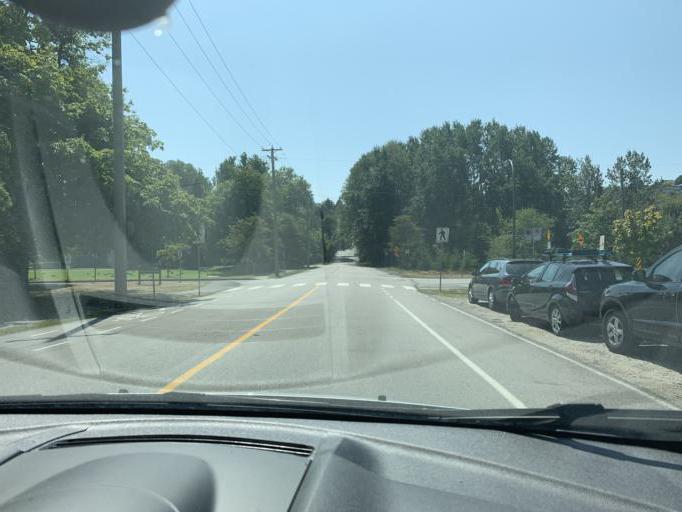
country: CA
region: British Columbia
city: West End
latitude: 49.2740
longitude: -123.2057
